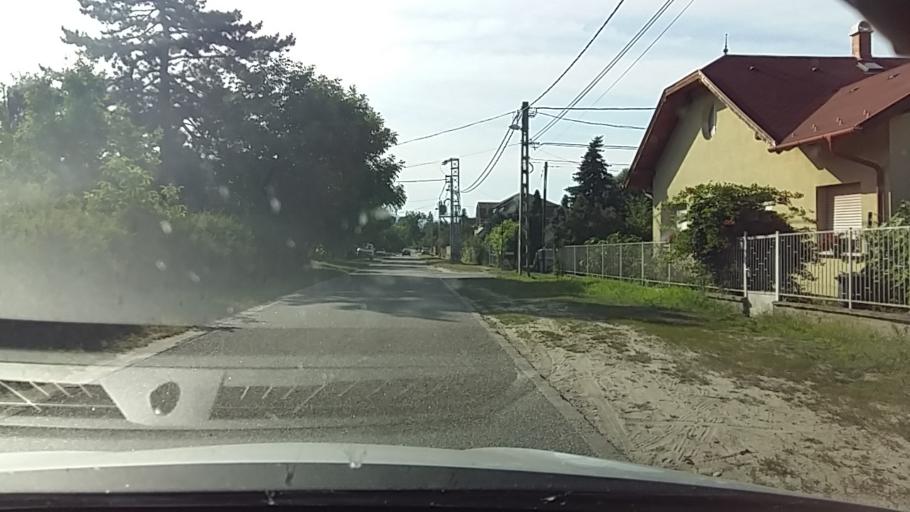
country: HU
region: Pest
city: God
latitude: 47.6982
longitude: 19.1491
